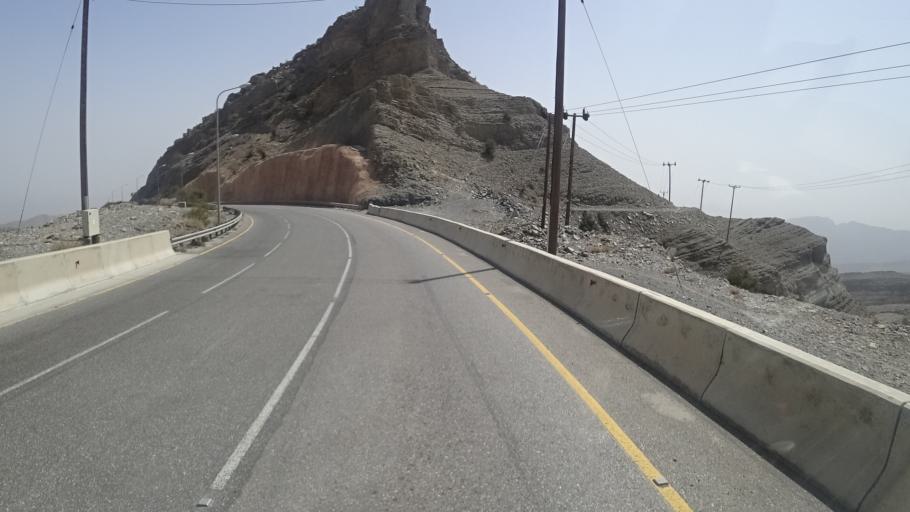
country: OM
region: Muhafazat ad Dakhiliyah
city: Izki
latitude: 23.0157
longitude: 57.6951
